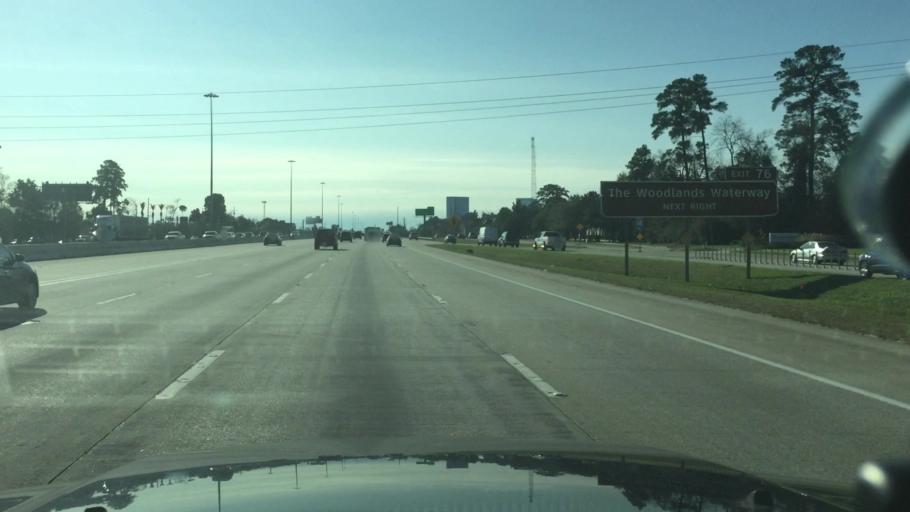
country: US
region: Texas
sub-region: Montgomery County
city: Shenandoah
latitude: 30.1869
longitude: -95.4529
